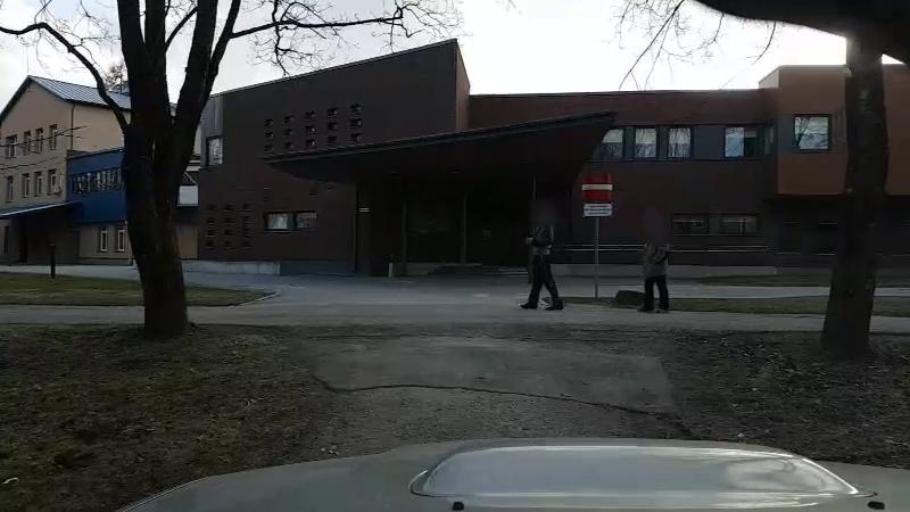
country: EE
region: Jaervamaa
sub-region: Paide linn
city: Paide
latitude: 58.8879
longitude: 25.5605
